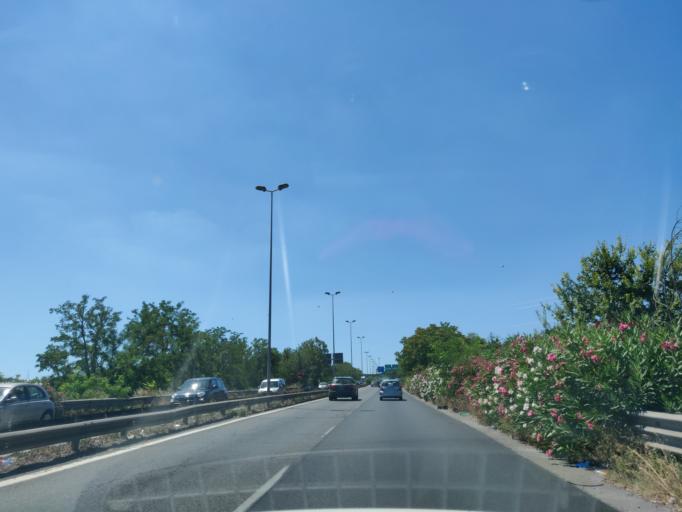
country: IT
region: Latium
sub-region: Citta metropolitana di Roma Capitale
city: Selcetta
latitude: 41.8078
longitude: 12.4568
